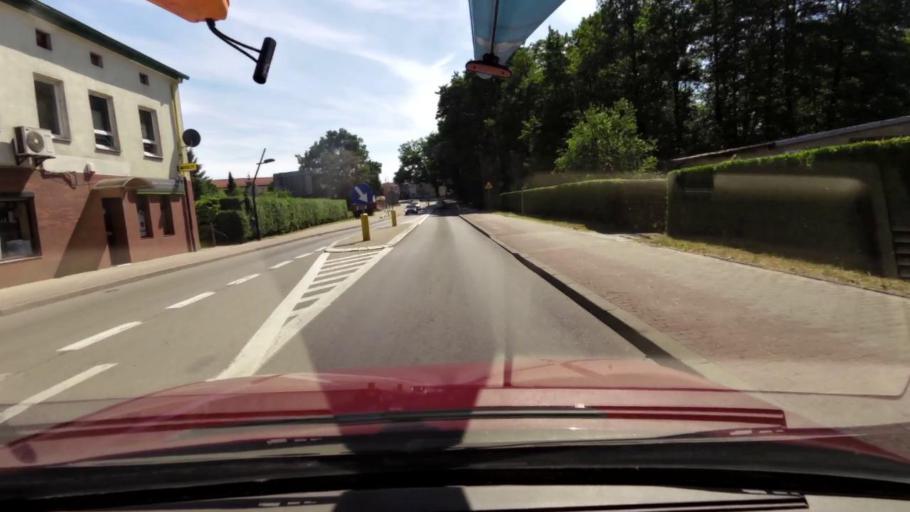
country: PL
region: Pomeranian Voivodeship
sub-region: Powiat slupski
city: Kobylnica
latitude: 54.4403
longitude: 16.9981
